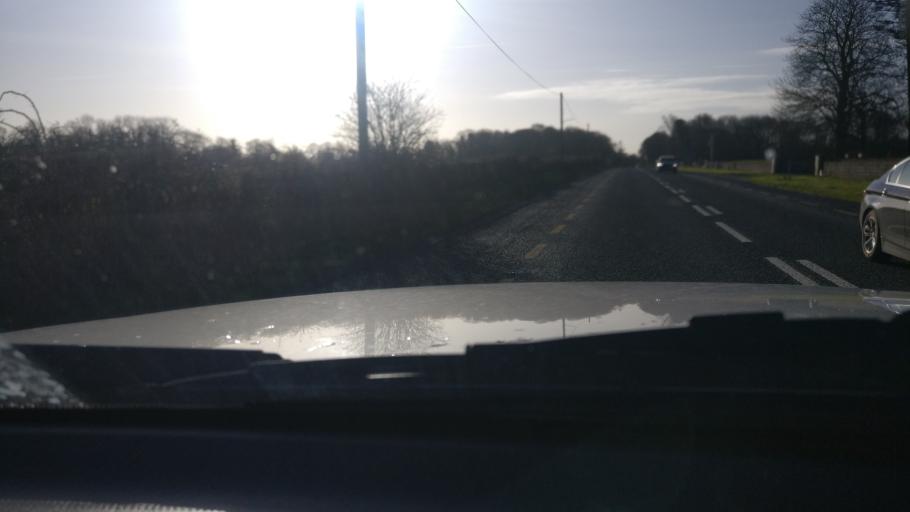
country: IE
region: Leinster
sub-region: An Iarmhi
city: Moate
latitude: 53.5958
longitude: -7.7159
